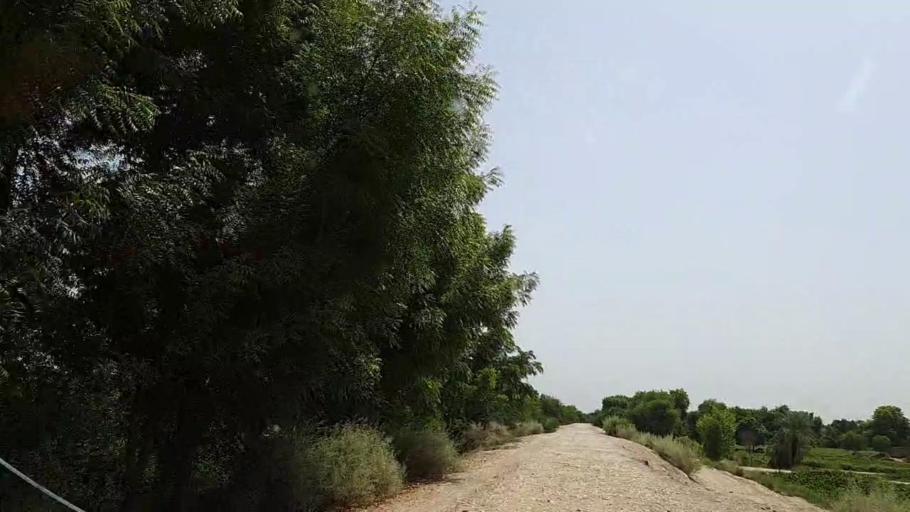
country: PK
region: Sindh
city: Tharu Shah
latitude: 27.0312
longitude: 68.1237
